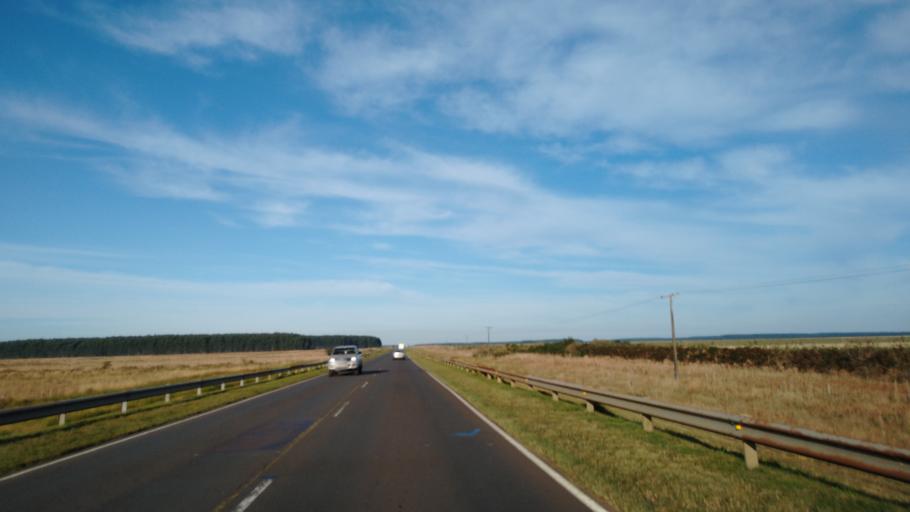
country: AR
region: Corrientes
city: Yapeyu
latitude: -29.3002
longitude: -56.7734
